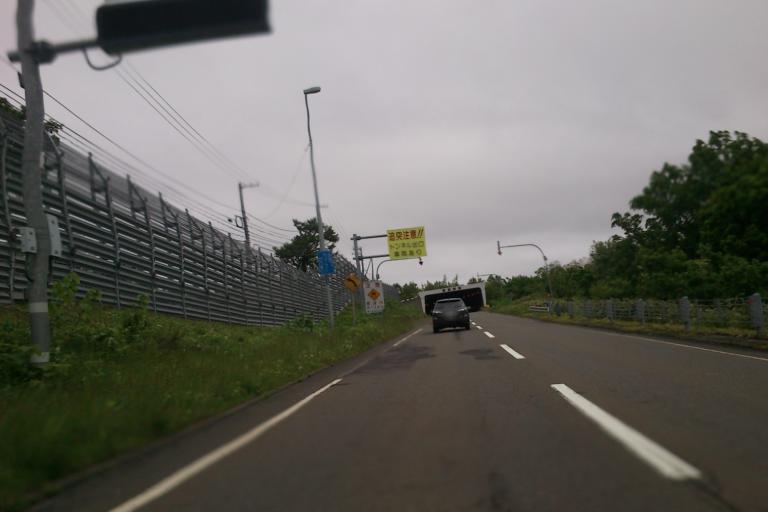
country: JP
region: Hokkaido
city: Ishikari
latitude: 43.3307
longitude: 141.4417
